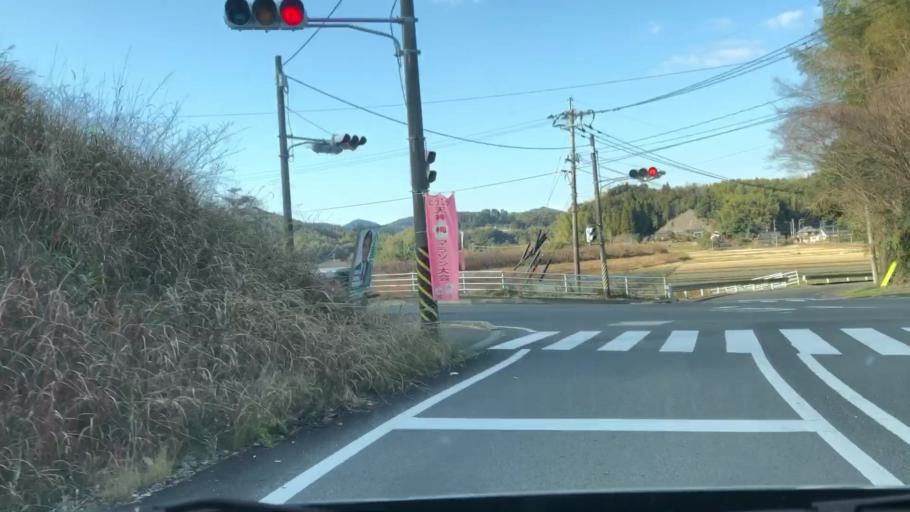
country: JP
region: Kagoshima
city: Satsumasendai
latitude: 31.8652
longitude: 130.3292
